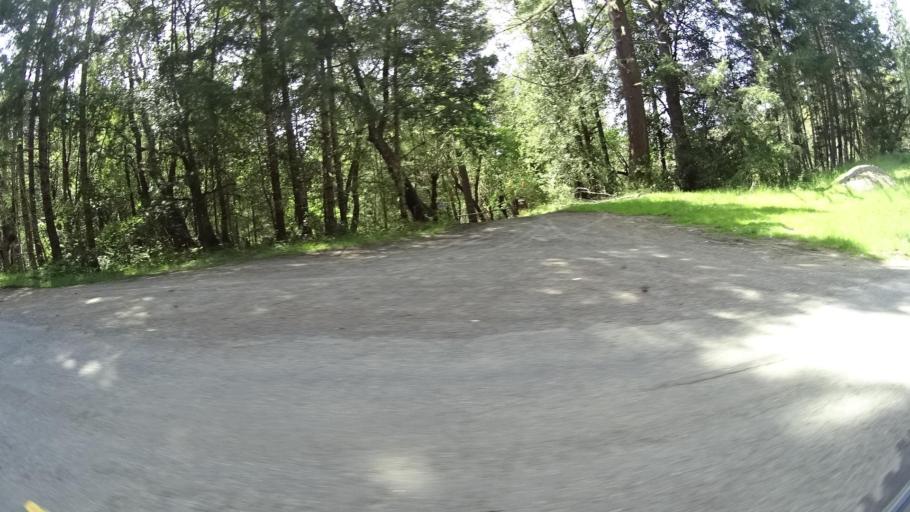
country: US
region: California
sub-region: Humboldt County
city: Redway
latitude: 40.4307
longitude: -123.7657
